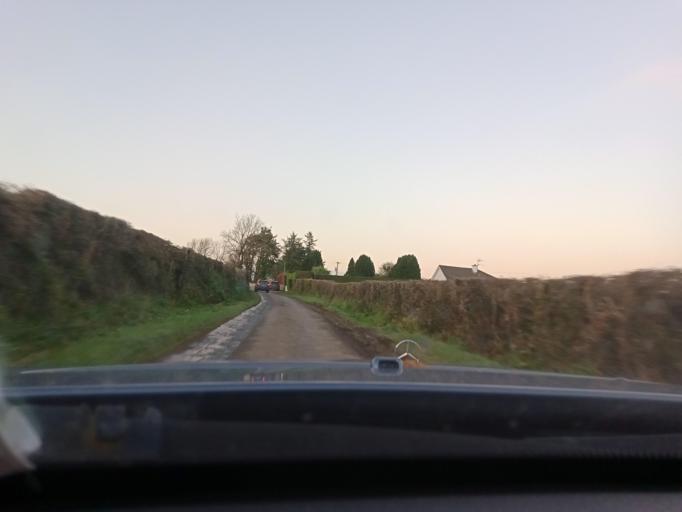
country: IE
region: Munster
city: Carrick-on-Suir
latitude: 52.4431
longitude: -7.3924
